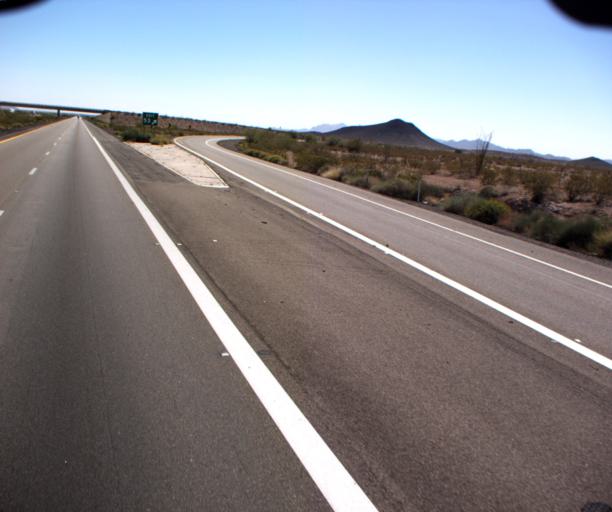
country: US
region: Arizona
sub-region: La Paz County
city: Salome
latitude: 33.6096
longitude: -113.6252
